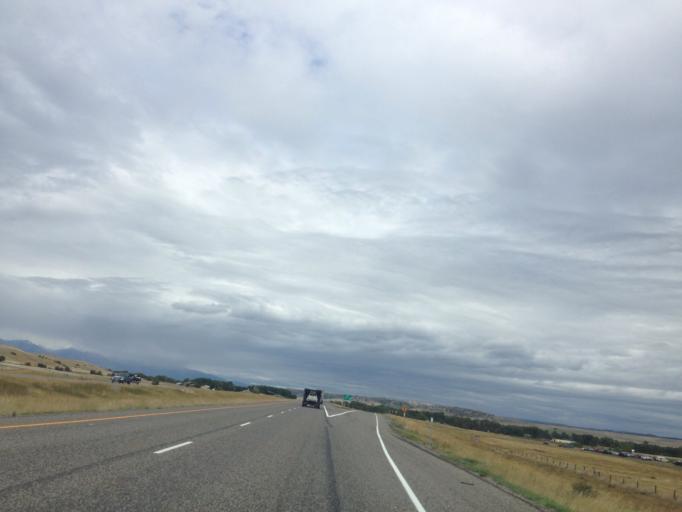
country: US
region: Montana
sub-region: Sweet Grass County
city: Big Timber
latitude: 45.7660
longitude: -109.7905
